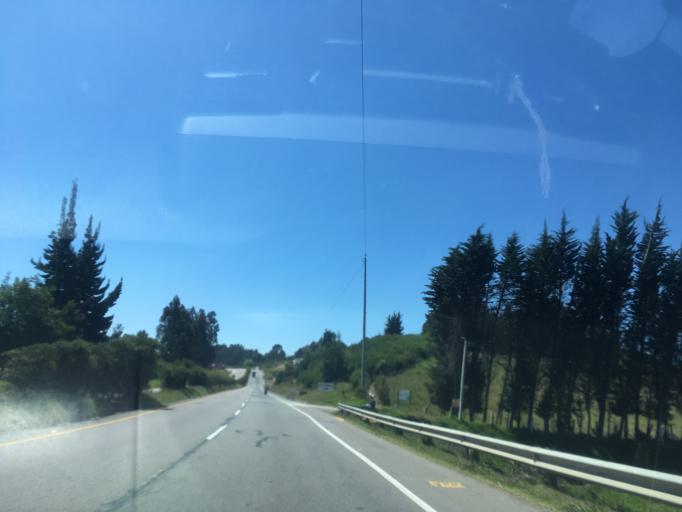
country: CO
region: Boyaca
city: Tuta
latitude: 5.6870
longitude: -73.2647
